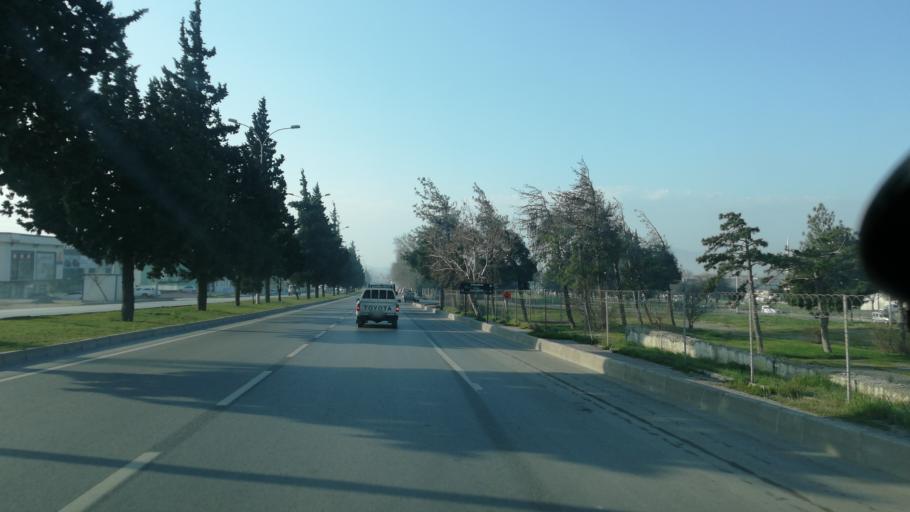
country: TR
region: Kahramanmaras
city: Kahramanmaras
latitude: 37.5648
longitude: 36.9240
